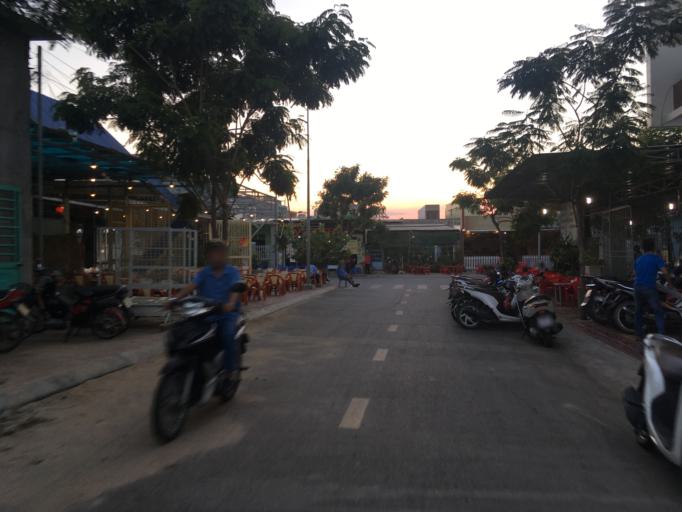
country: VN
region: Ninh Thuan
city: Phan Rang-Thap Cham
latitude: 11.5677
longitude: 108.9968
